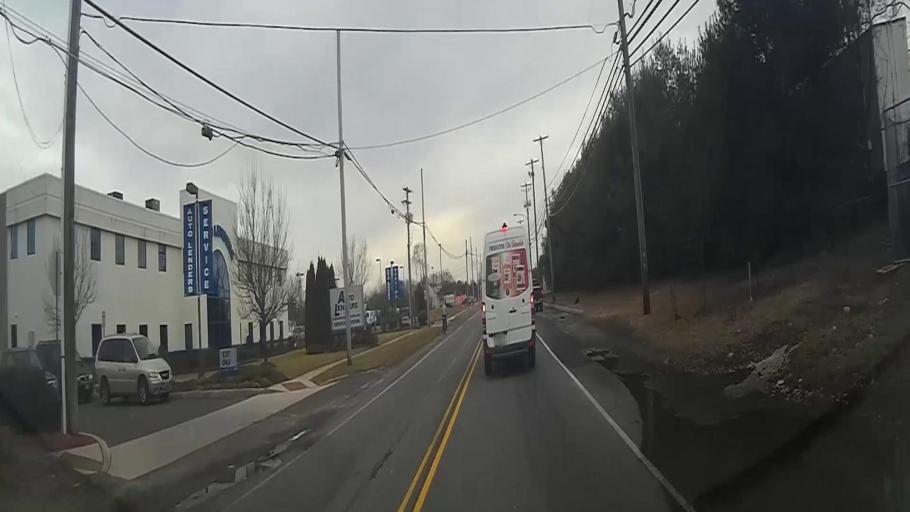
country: US
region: New Jersey
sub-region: Camden County
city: Berlin
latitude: 39.7827
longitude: -74.9503
